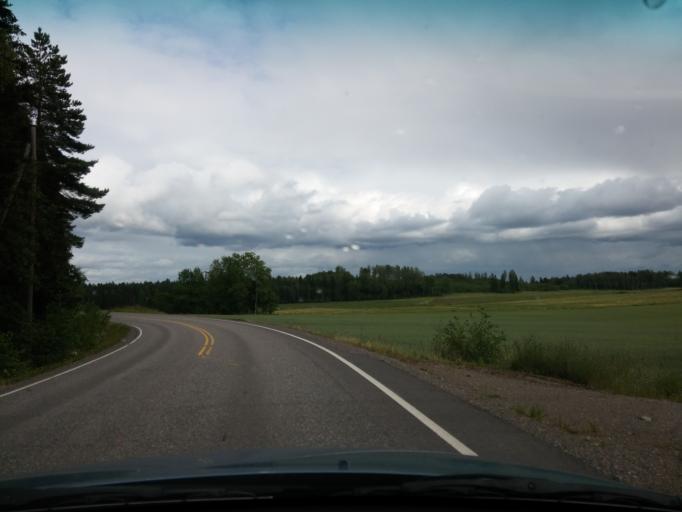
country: FI
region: Uusimaa
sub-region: Porvoo
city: Askola
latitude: 60.5429
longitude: 25.6401
